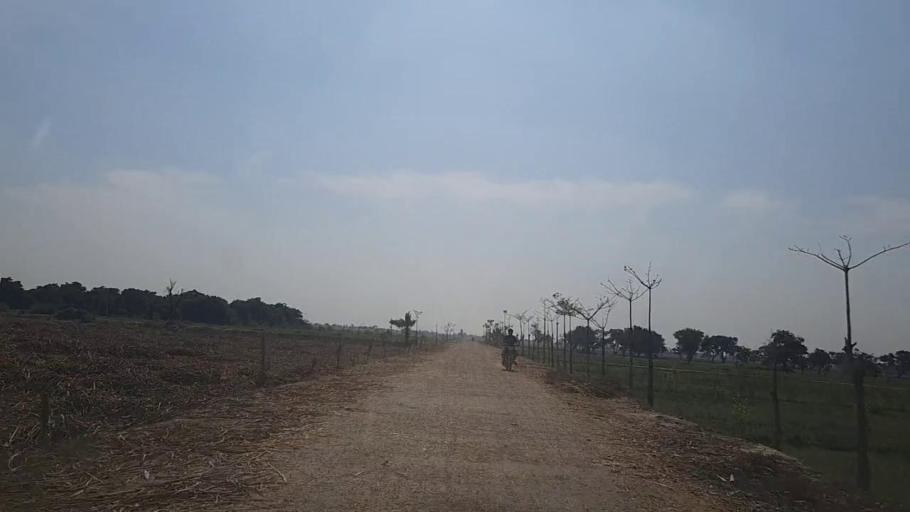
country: PK
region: Sindh
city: Mirpur Khas
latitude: 25.4935
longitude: 68.9440
